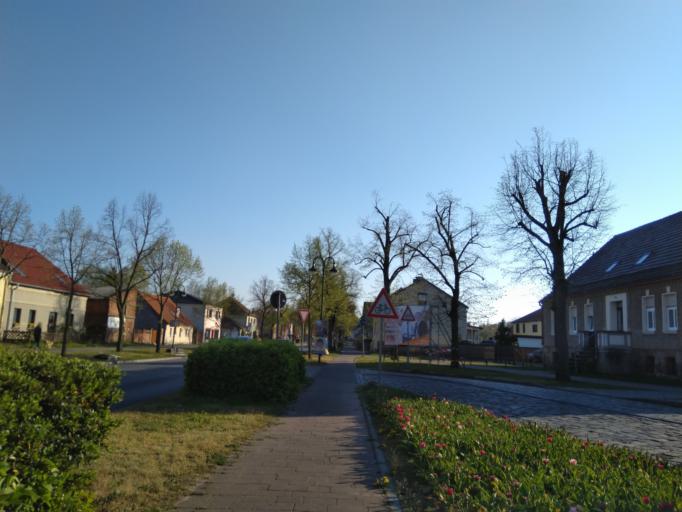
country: DE
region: Berlin
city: Buch
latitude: 52.6543
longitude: 13.5429
